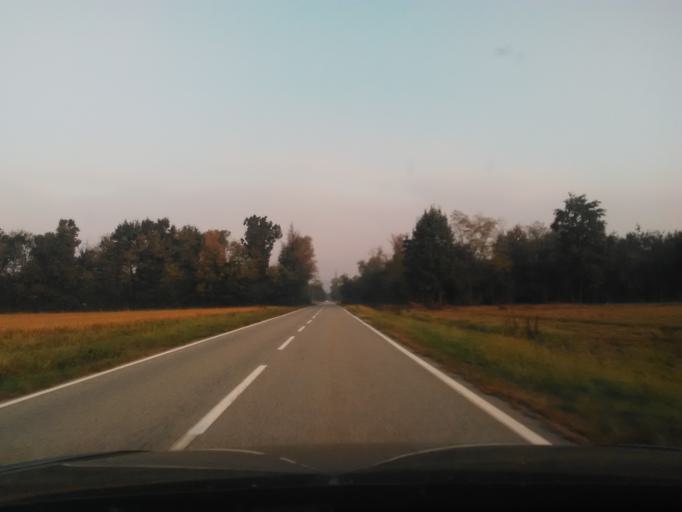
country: IT
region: Piedmont
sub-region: Provincia di Vercelli
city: Rovasenda
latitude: 45.5634
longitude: 8.2971
